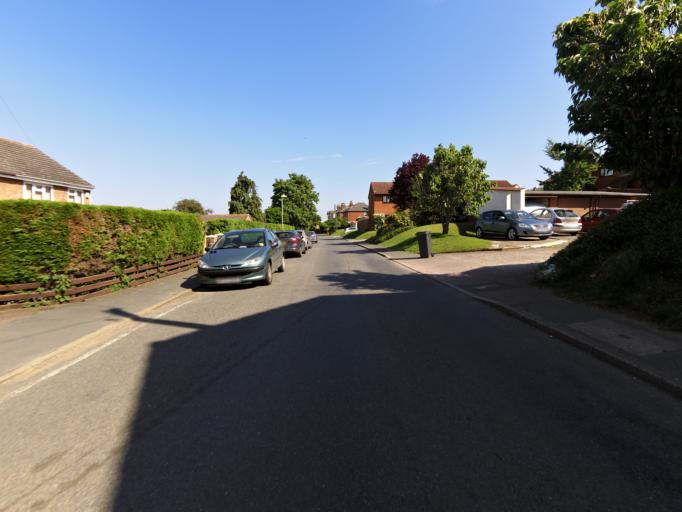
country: GB
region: England
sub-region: Suffolk
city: Bramford
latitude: 52.0783
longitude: 1.1063
